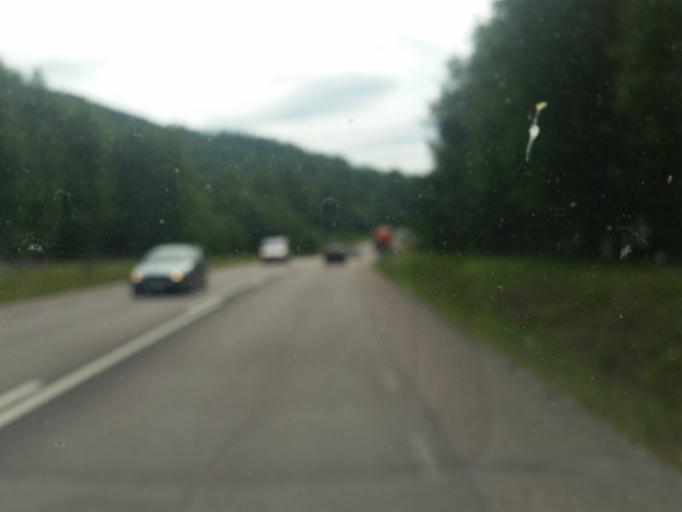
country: SE
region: Dalarna
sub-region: Gagnefs Kommun
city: Djuras
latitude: 60.5466
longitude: 15.2761
